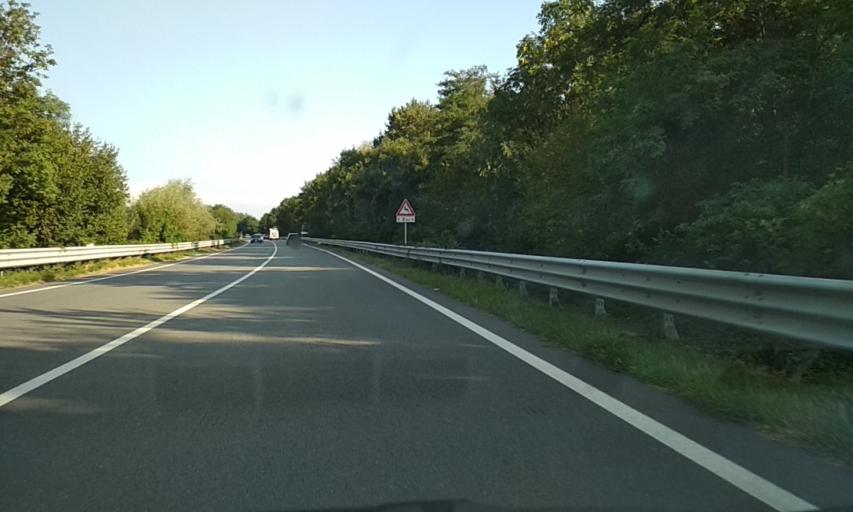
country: IT
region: Piedmont
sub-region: Provincia di Torino
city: San Colombano Belmonte
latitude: 45.4076
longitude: 7.6260
